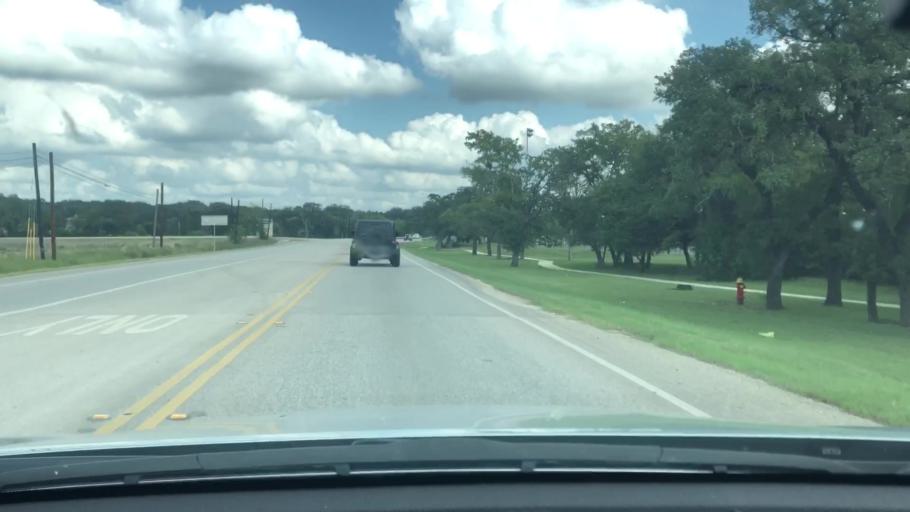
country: US
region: Texas
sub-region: Kendall County
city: Boerne
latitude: 29.7885
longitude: -98.7041
